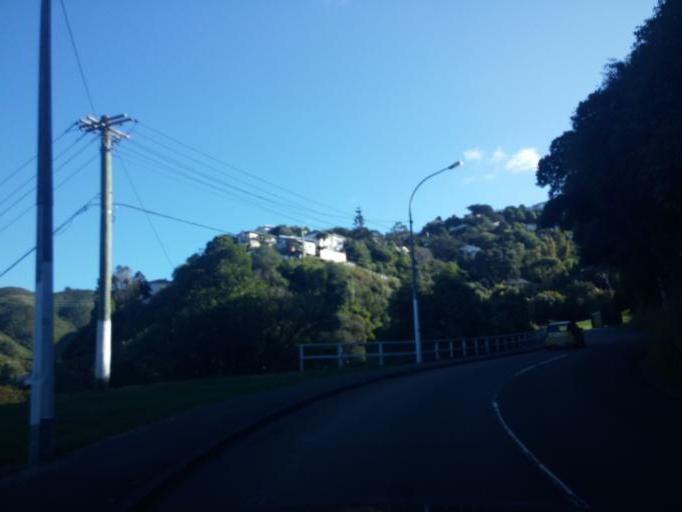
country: NZ
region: Wellington
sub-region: Wellington City
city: Kelburn
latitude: -41.2938
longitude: 174.7592
